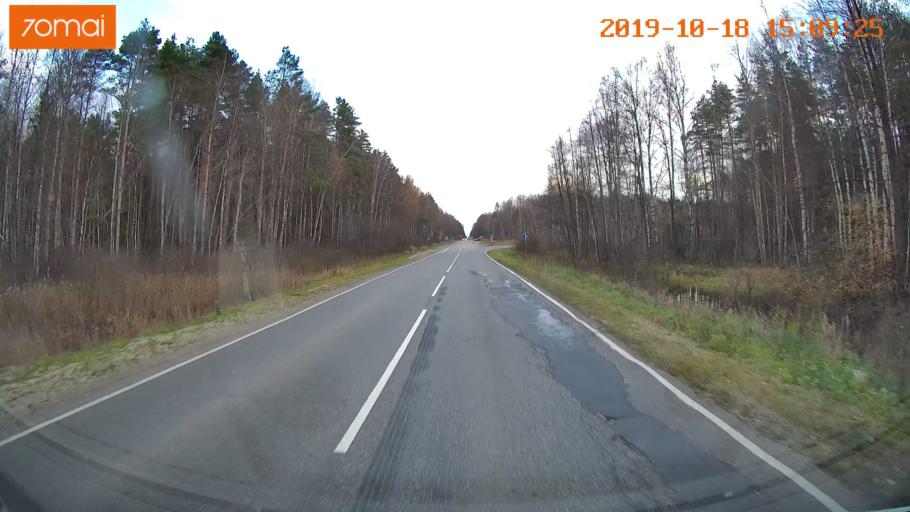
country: RU
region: Vladimir
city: Gus'-Khrustal'nyy
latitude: 55.5659
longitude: 40.6209
